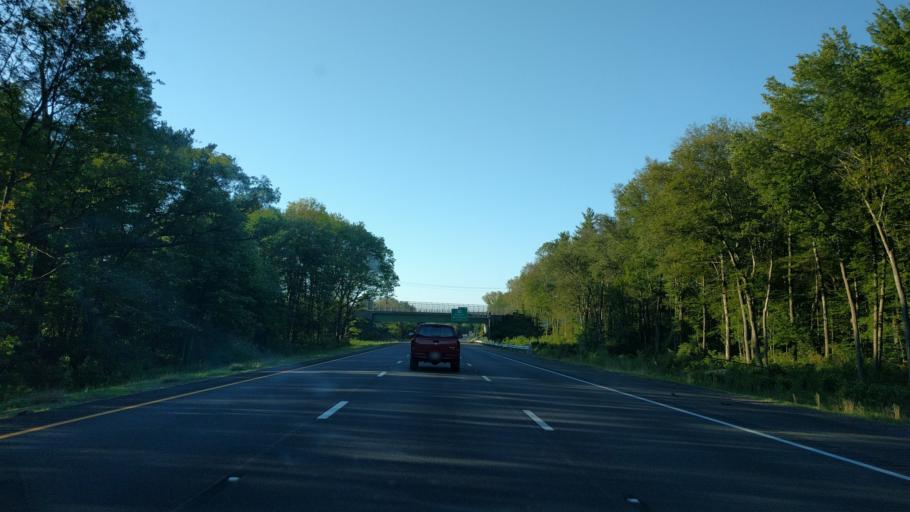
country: US
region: Massachusetts
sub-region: Norfolk County
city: Bellingham
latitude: 42.1284
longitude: -71.4754
